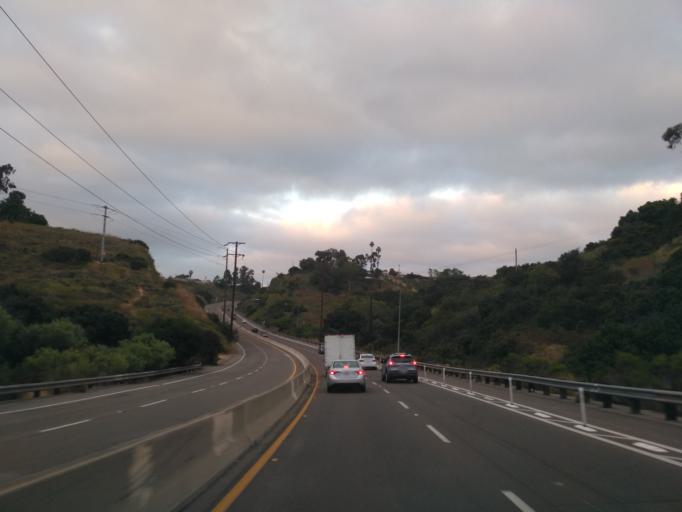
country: US
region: California
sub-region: San Diego County
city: La Jolla
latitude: 32.8123
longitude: -117.1967
